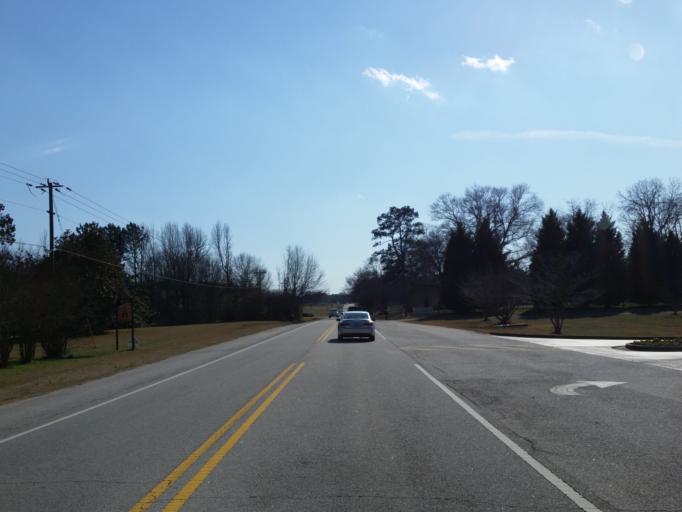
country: US
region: Georgia
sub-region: Clayton County
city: Lovejoy
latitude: 33.4330
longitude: -84.2748
